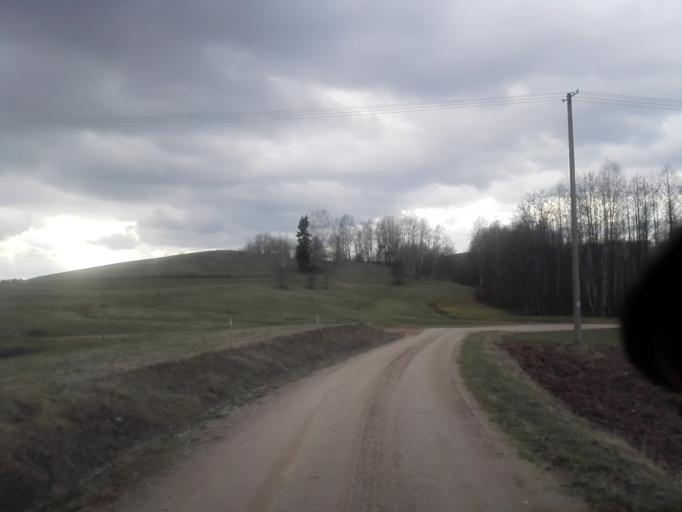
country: PL
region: Podlasie
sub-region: Suwalki
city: Suwalki
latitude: 54.2584
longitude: 22.9477
